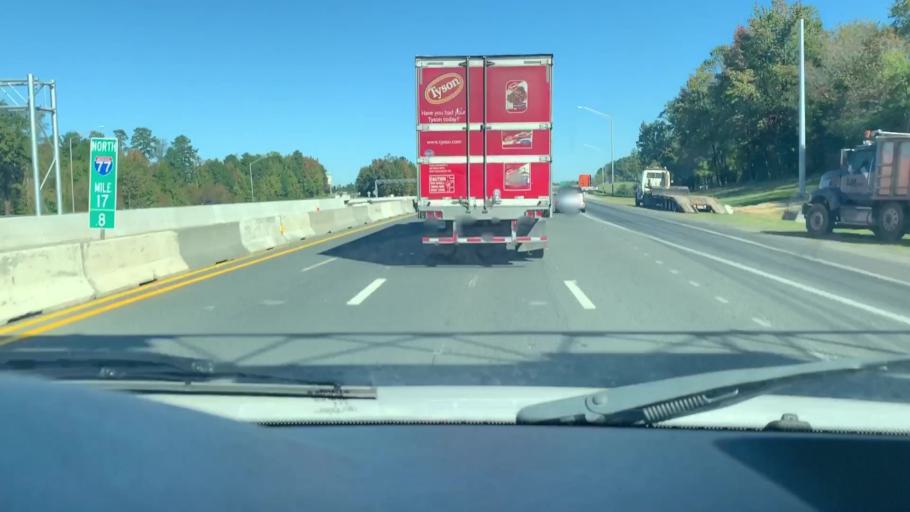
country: US
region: North Carolina
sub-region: Mecklenburg County
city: Huntersville
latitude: 35.3430
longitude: -80.8483
